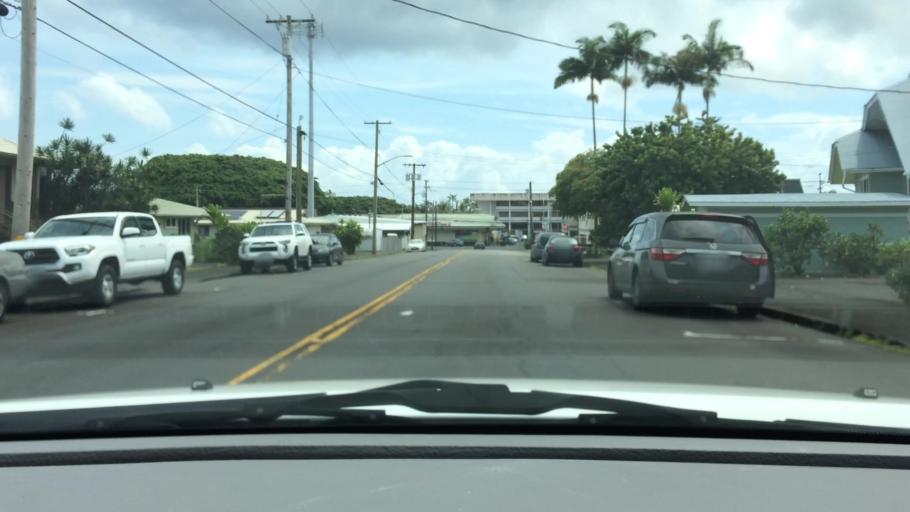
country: US
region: Hawaii
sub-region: Hawaii County
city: Hilo
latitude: 19.7174
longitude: -155.0822
